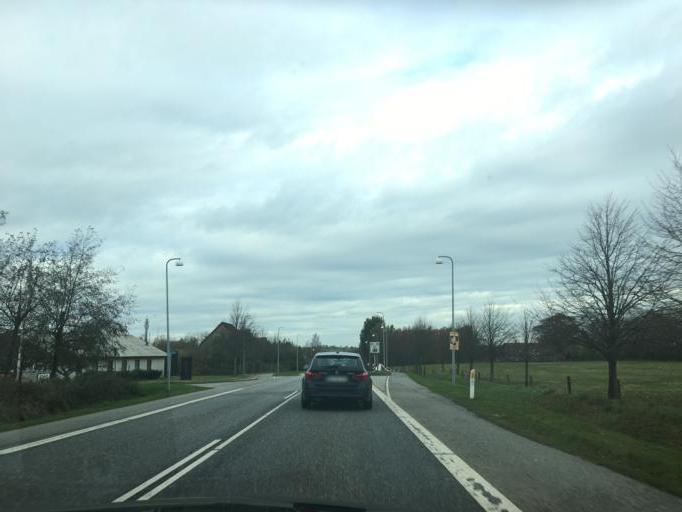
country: DK
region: South Denmark
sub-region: Vejle Kommune
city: Vejle
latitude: 55.6533
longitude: 9.5041
